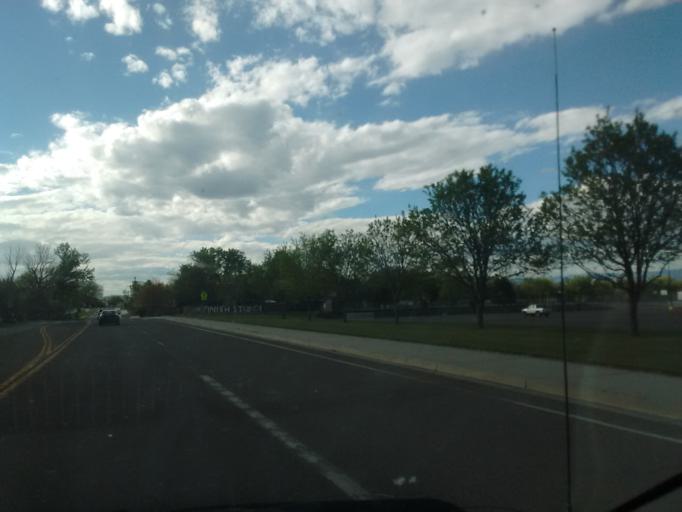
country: US
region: Colorado
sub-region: Mesa County
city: Redlands
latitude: 39.0839
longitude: -108.6450
